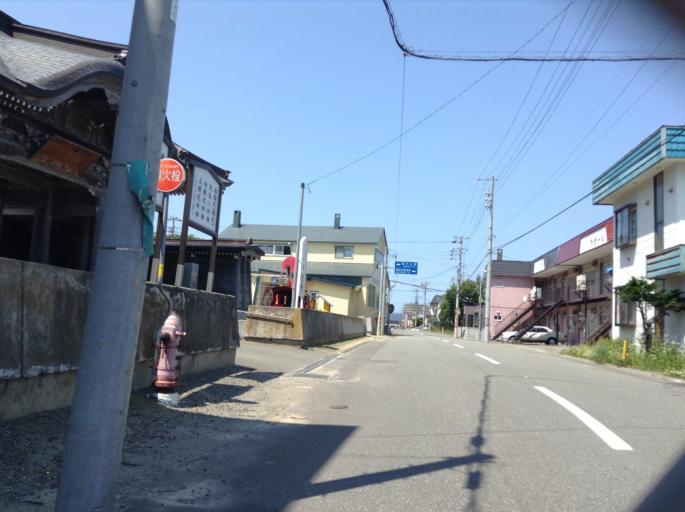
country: JP
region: Hokkaido
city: Wakkanai
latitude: 45.4227
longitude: 141.6715
